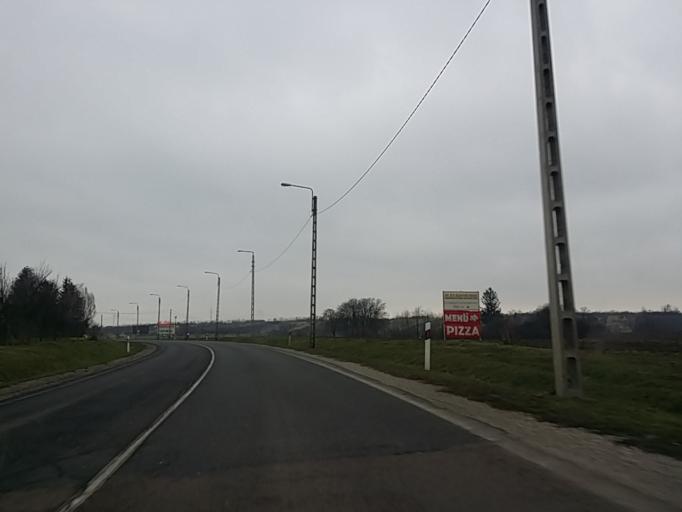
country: HU
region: Borsod-Abauj-Zemplen
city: Mezokeresztes
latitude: 47.8853
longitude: 20.6802
